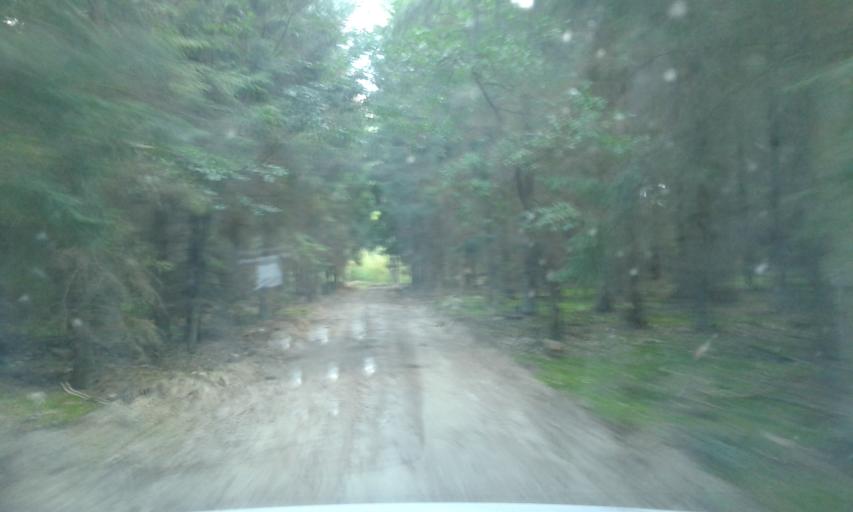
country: PL
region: West Pomeranian Voivodeship
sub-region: Powiat stargardzki
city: Dolice
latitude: 53.2294
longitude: 15.2490
